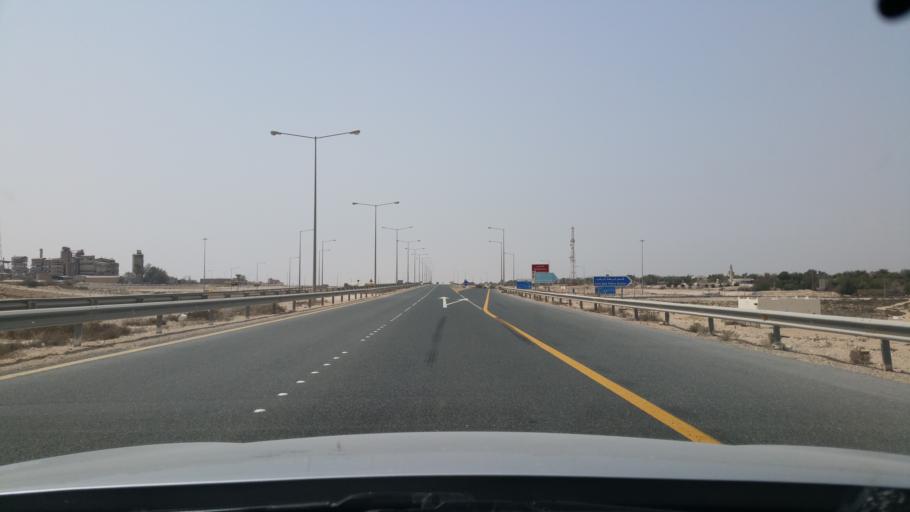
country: QA
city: Umm Bab
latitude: 25.2145
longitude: 50.8069
